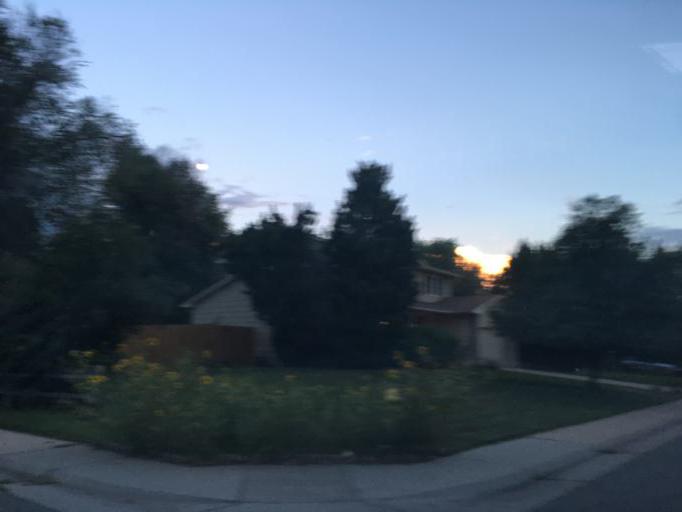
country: US
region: Colorado
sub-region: Adams County
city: Aurora
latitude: 39.6878
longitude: -104.8506
